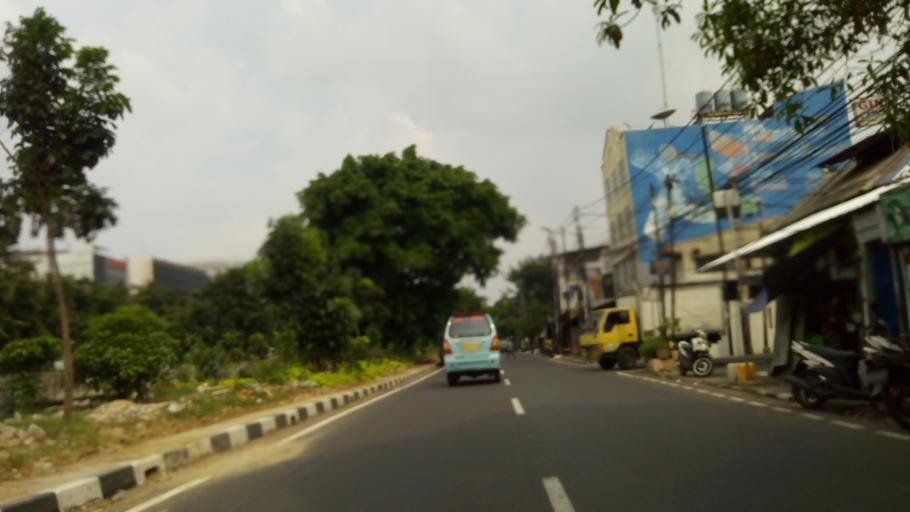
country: ID
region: Jakarta Raya
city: Jakarta
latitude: -6.1550
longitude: 106.8358
